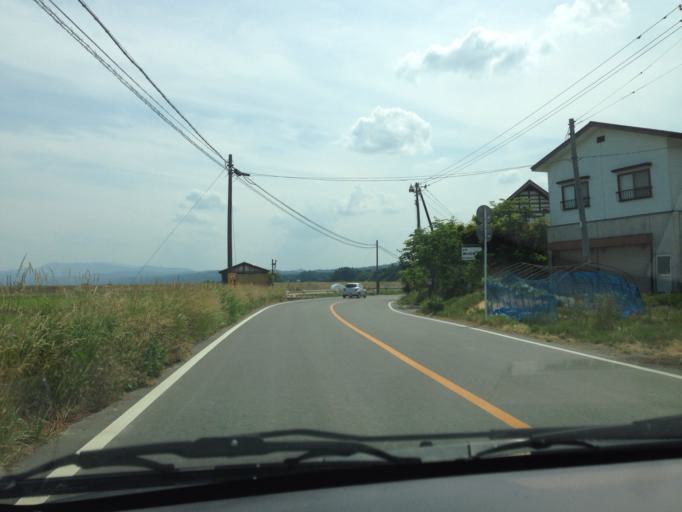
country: JP
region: Fukushima
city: Kitakata
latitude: 37.6107
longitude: 139.8254
